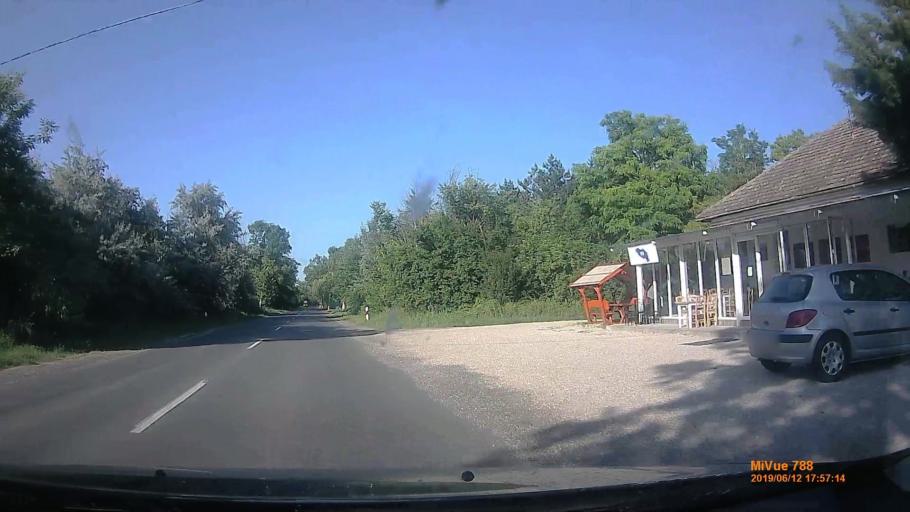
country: HU
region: Csongrad
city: Roszke
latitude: 46.1965
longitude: 20.0087
